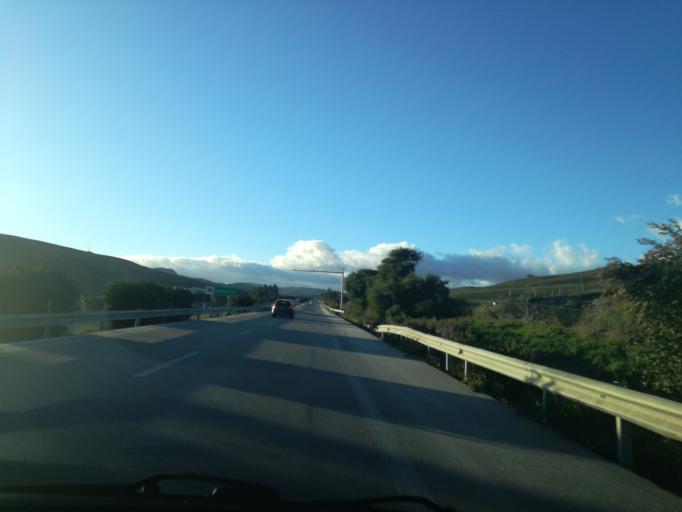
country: IT
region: Sicily
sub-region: Palermo
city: Castellana Sicula
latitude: 37.7391
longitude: 14.0060
